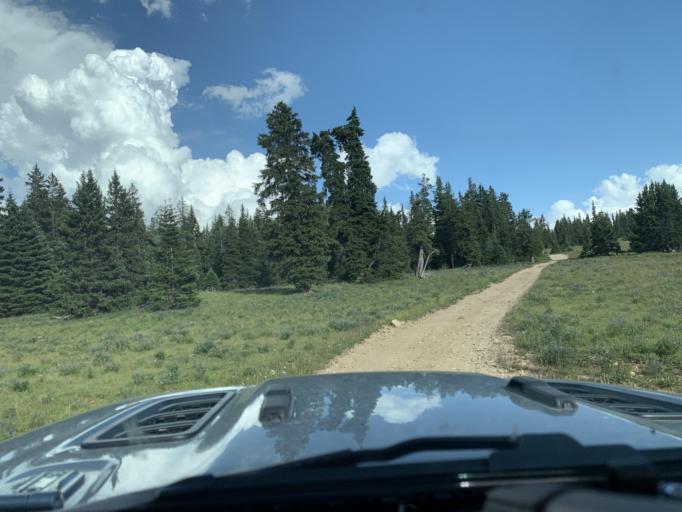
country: US
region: Colorado
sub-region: Lake County
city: Leadville North
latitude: 39.3074
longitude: -106.2863
